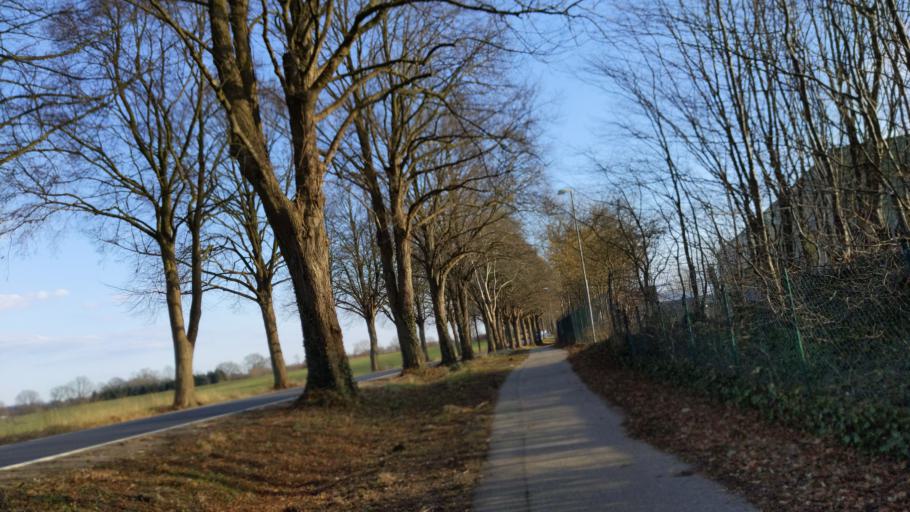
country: DE
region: Schleswig-Holstein
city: Ratekau
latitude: 53.9590
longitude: 10.7228
